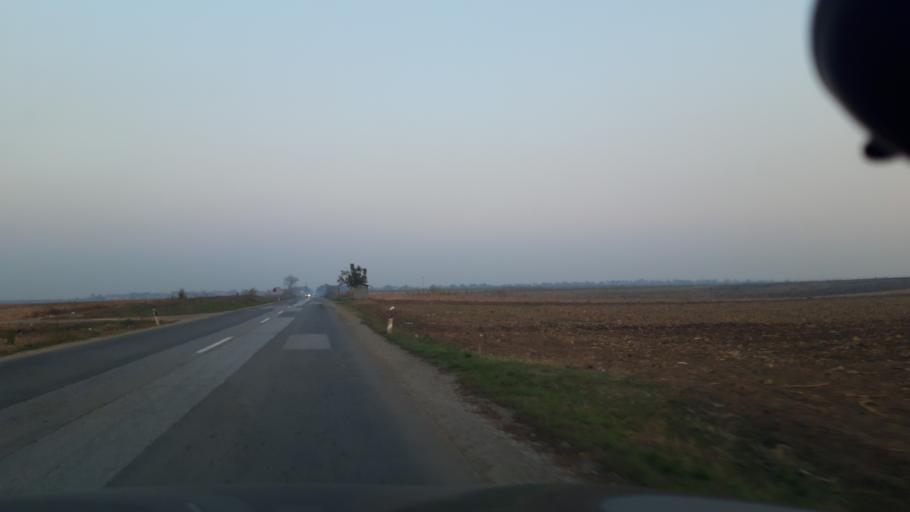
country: RS
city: Putinci
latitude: 44.9983
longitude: 19.9490
